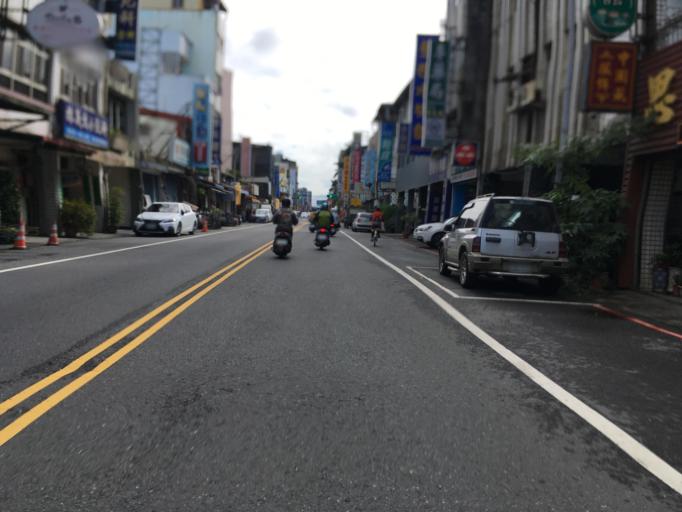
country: TW
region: Taiwan
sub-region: Yilan
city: Yilan
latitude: 24.7508
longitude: 121.7535
